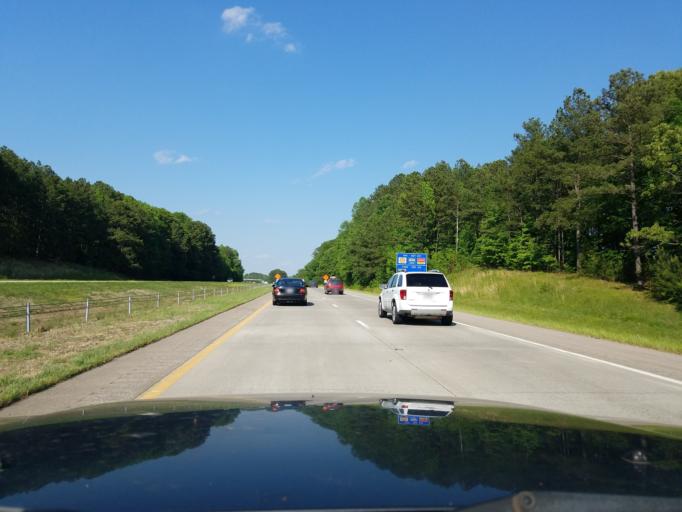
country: US
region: North Carolina
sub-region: Vance County
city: South Henderson
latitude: 36.3223
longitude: -78.4588
